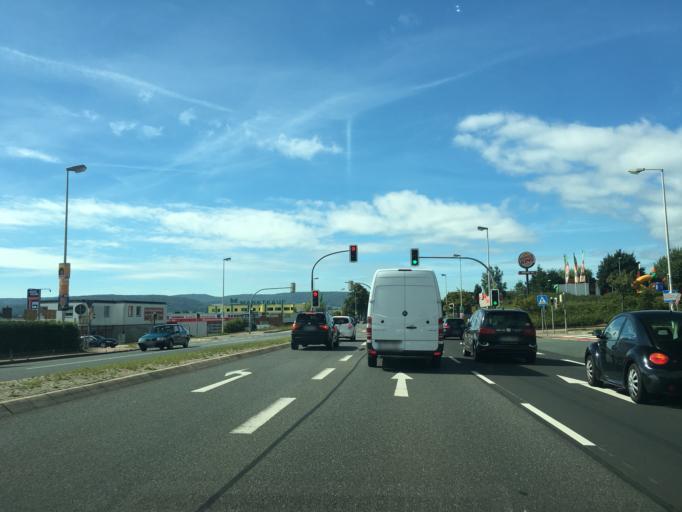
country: DE
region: Lower Saxony
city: Hameln
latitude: 52.0852
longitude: 9.3439
